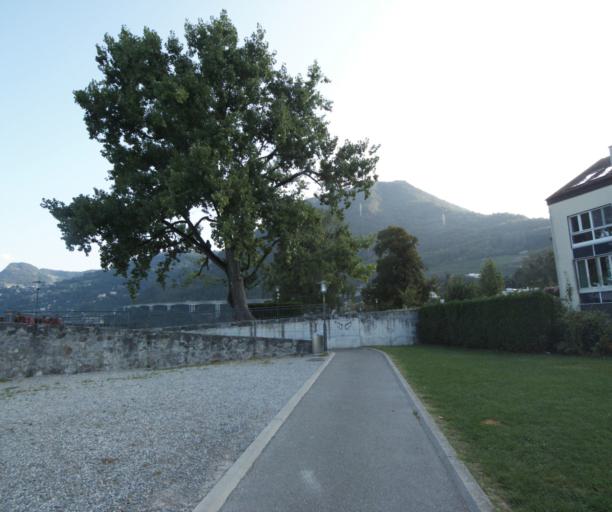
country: CH
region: Vaud
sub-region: Aigle District
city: Villeneuve
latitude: 46.4017
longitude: 6.9251
